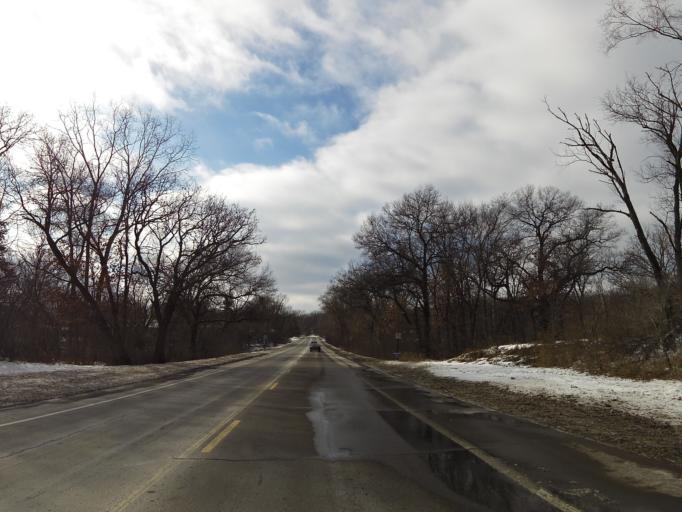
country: US
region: Minnesota
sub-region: Hennepin County
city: Minnetonka Mills
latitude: 44.9202
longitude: -93.4366
